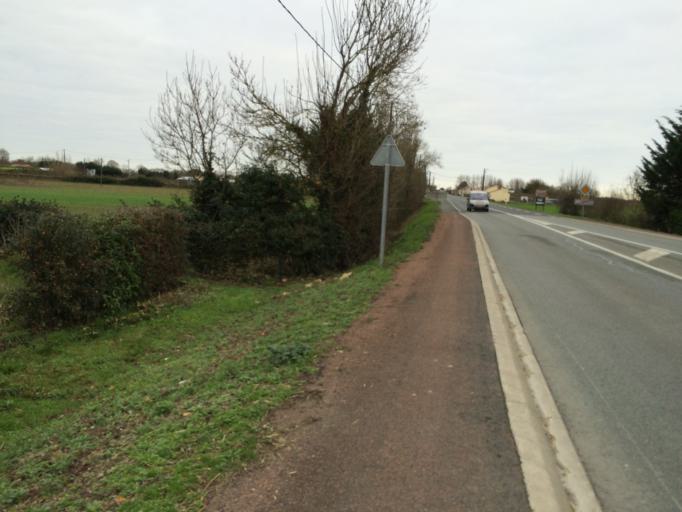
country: FR
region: Pays de la Loire
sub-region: Departement de la Vendee
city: Chaille-les-Marais
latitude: 46.3780
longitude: -1.0134
